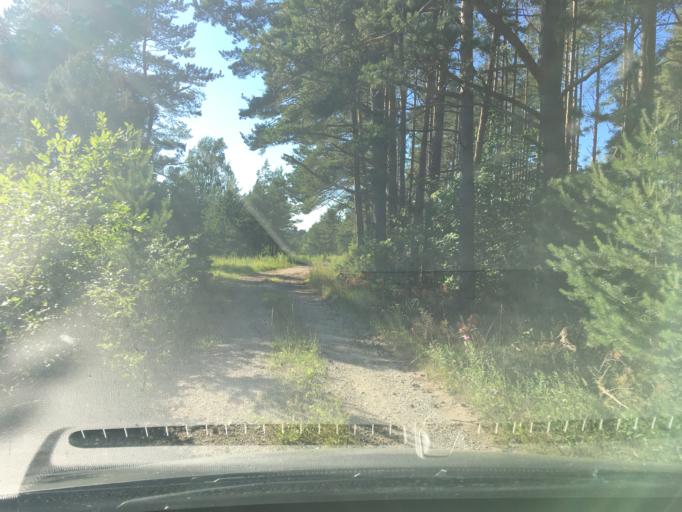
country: EE
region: Laeaene
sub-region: Lihula vald
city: Lihula
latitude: 58.5888
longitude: 23.7418
